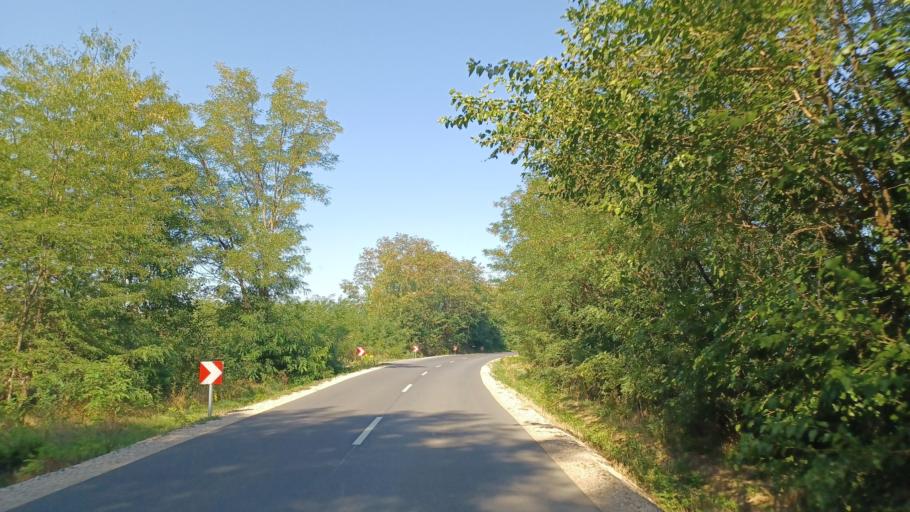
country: HU
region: Fejer
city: Cece
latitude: 46.7524
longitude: 18.6699
